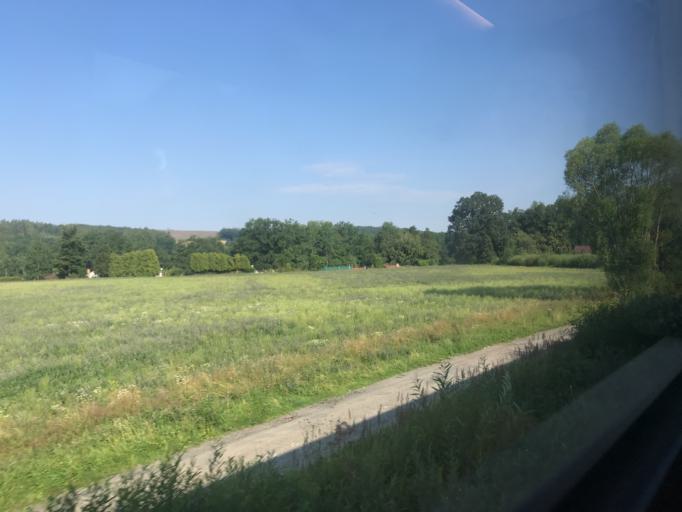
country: CZ
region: Jihocesky
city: Sobeslav
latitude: 49.2695
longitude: 14.7049
